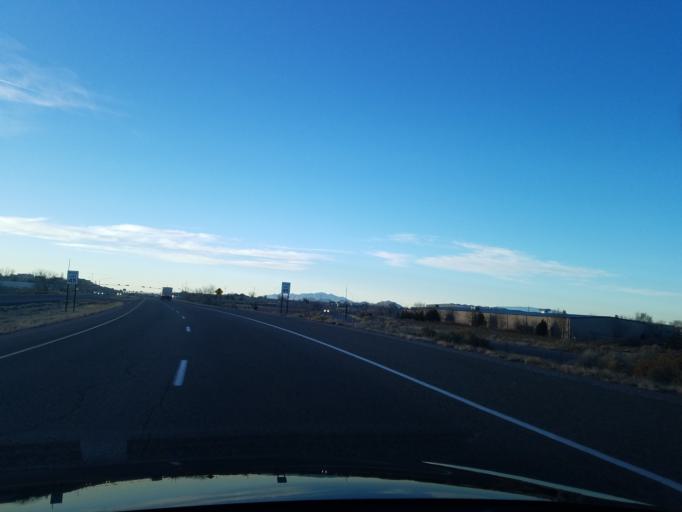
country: US
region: New Mexico
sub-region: Santa Fe County
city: Agua Fria
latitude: 35.6353
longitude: -106.0713
